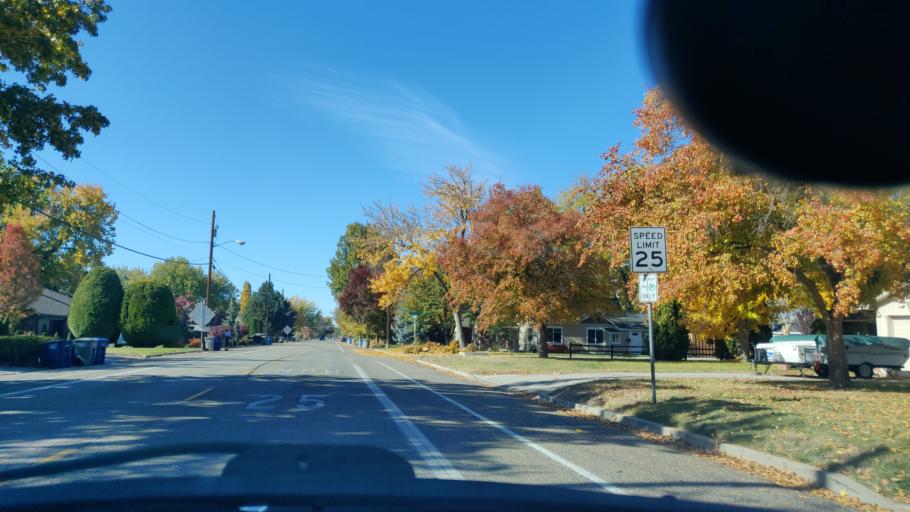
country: US
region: Idaho
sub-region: Ada County
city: Garden City
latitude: 43.5935
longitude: -116.2293
